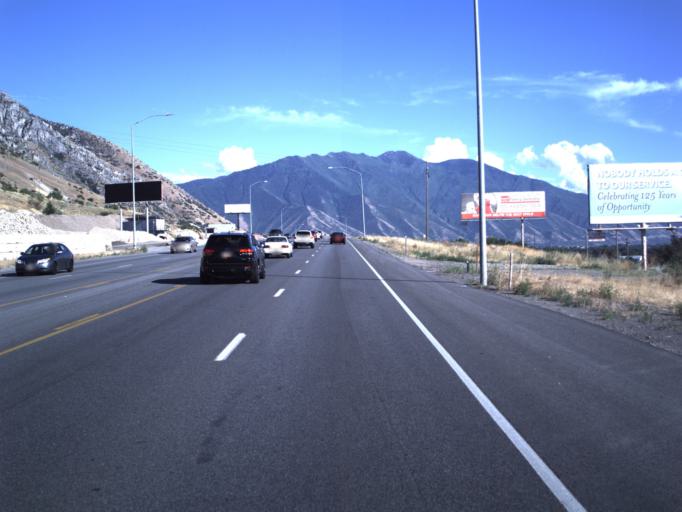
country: US
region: Utah
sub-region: Utah County
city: Springville
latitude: 40.1971
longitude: -111.6172
